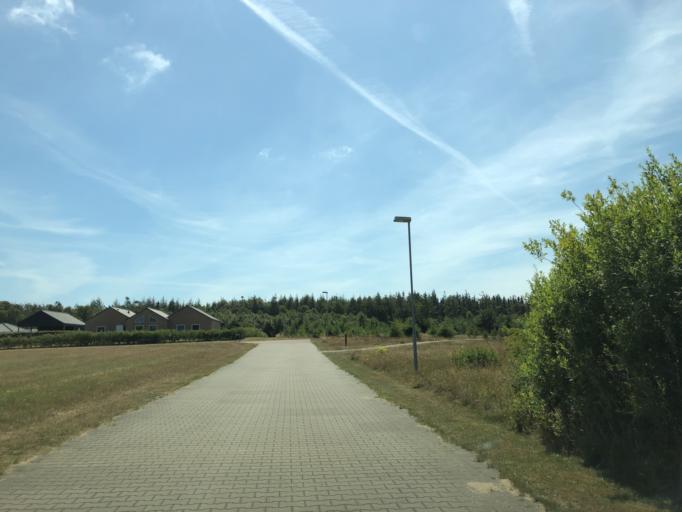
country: DK
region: Central Jutland
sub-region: Holstebro Kommune
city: Ulfborg
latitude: 56.2677
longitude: 8.3096
